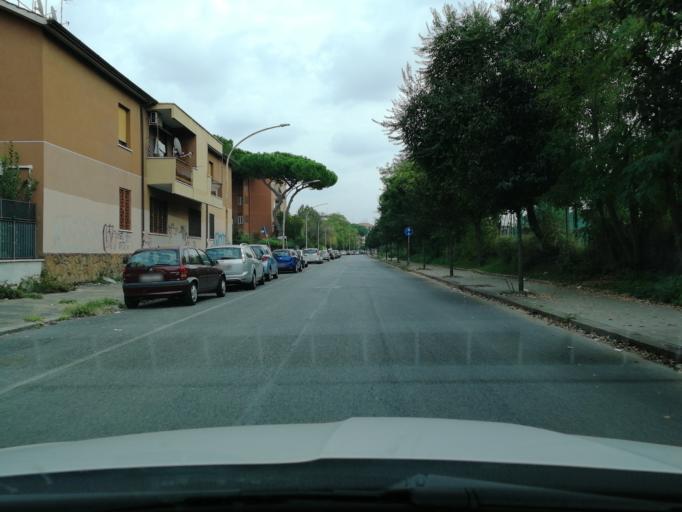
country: IT
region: Latium
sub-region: Citta metropolitana di Roma Capitale
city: Rome
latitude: 41.8559
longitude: 12.5538
